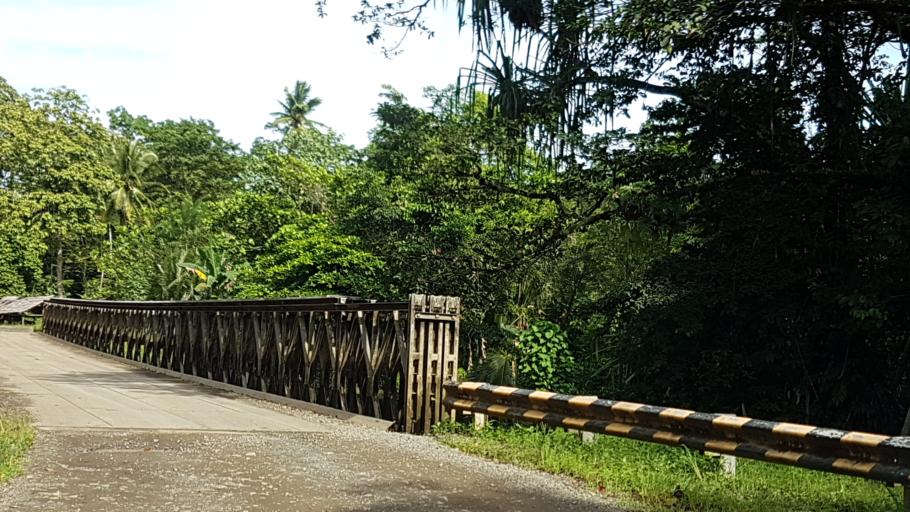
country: PG
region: Milne Bay
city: Alotau
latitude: -10.3386
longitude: 150.6069
